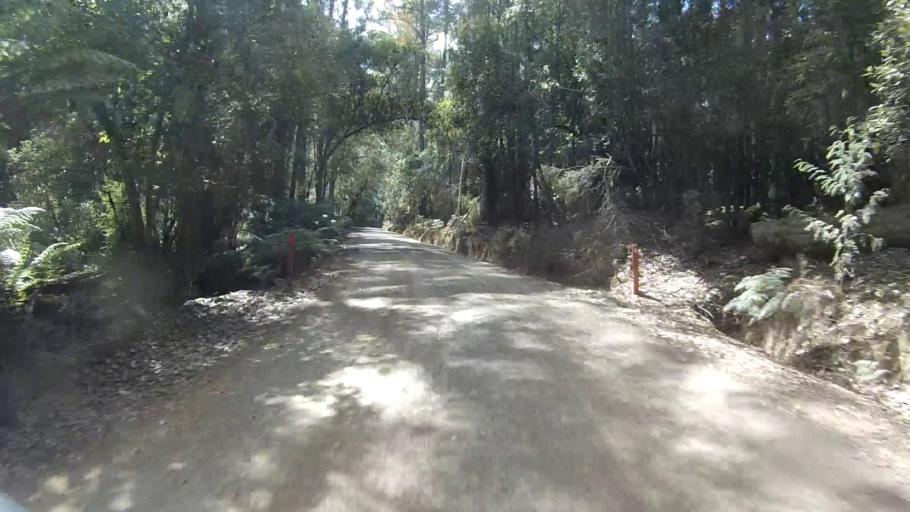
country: AU
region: Tasmania
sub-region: Derwent Valley
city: New Norfolk
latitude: -42.6829
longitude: 146.7088
